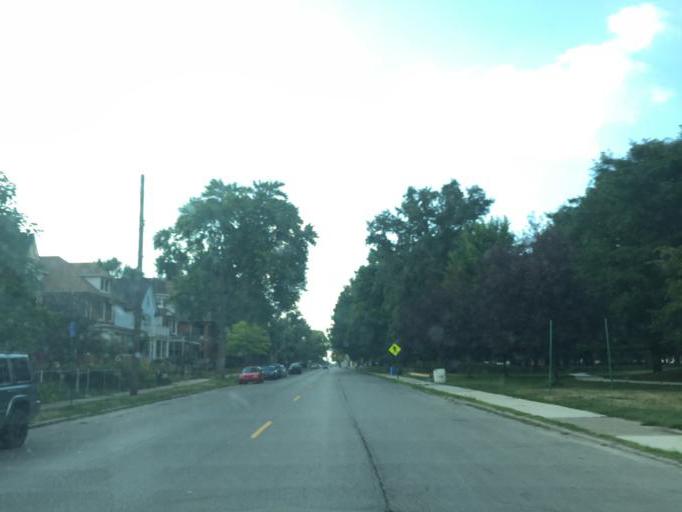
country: US
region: Michigan
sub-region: Wayne County
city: Detroit
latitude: 42.3179
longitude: -83.0941
